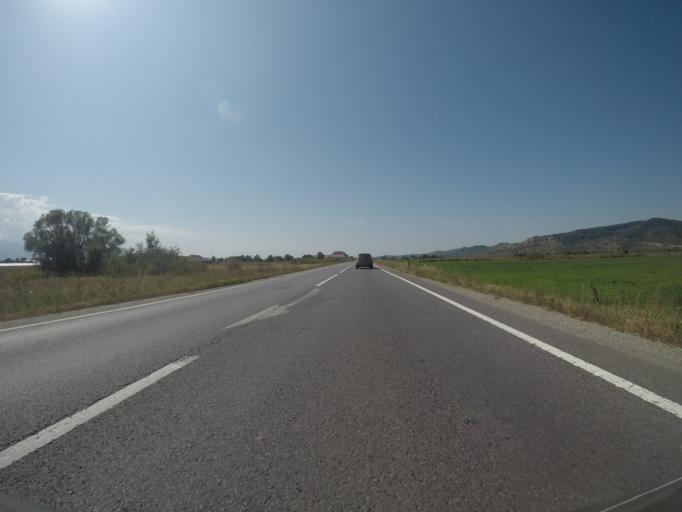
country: RO
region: Brasov
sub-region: Comuna Vistea de Jos
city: Vistea de Jos
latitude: 45.7965
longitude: 24.7331
